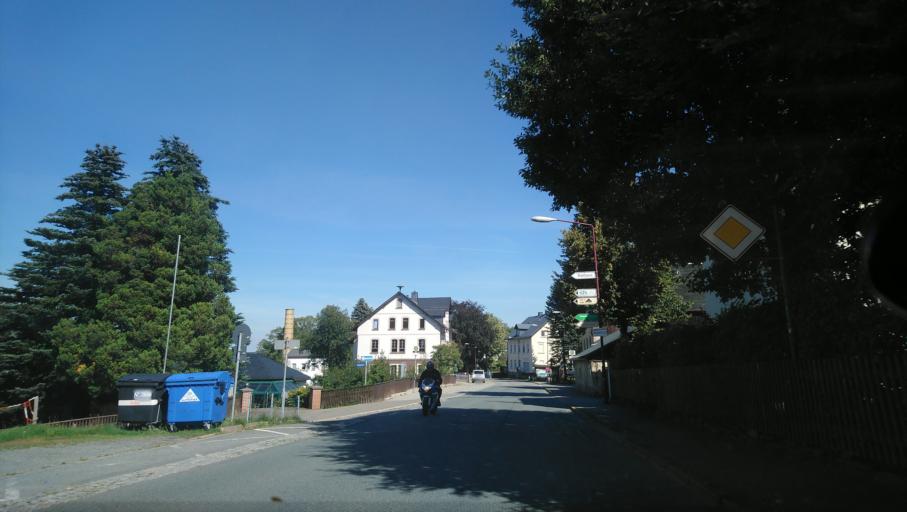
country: DE
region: Saxony
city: Crottendorf
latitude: 50.5128
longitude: 12.9917
